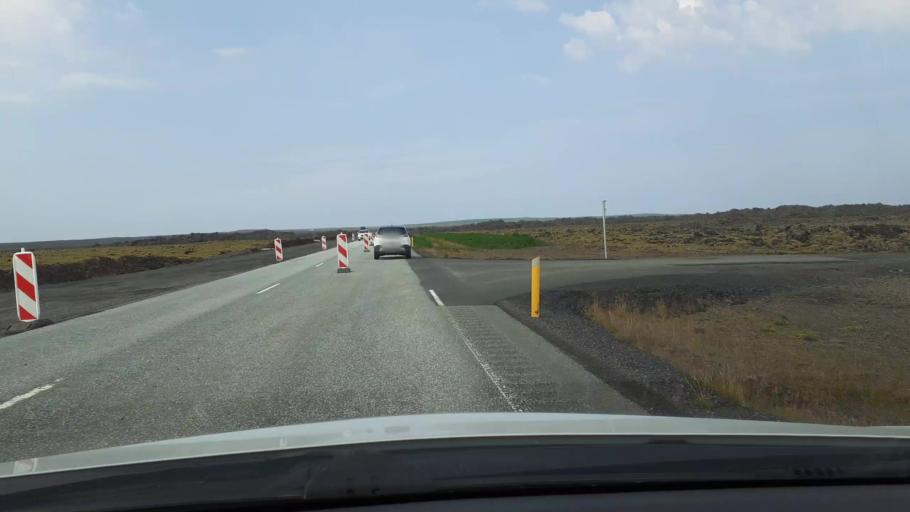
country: IS
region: Southern Peninsula
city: Vogar
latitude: 63.9227
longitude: -22.4221
